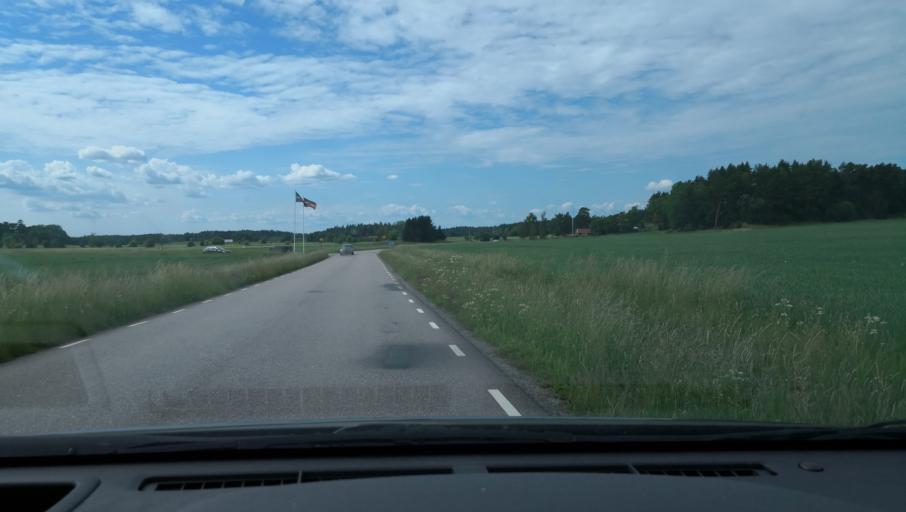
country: SE
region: Uppsala
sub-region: Uppsala Kommun
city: Uppsala
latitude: 59.8137
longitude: 17.5044
